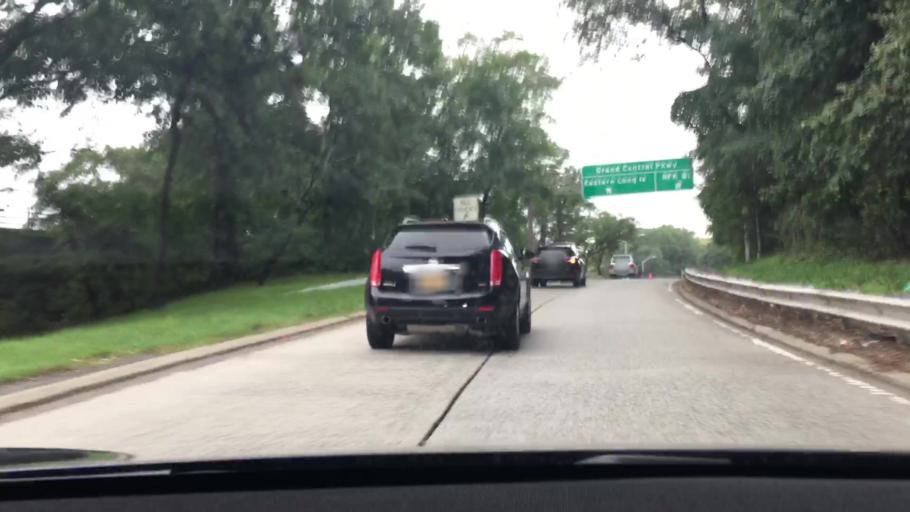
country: US
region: New York
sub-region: Nassau County
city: Bellerose Terrace
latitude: 40.7457
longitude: -73.7356
